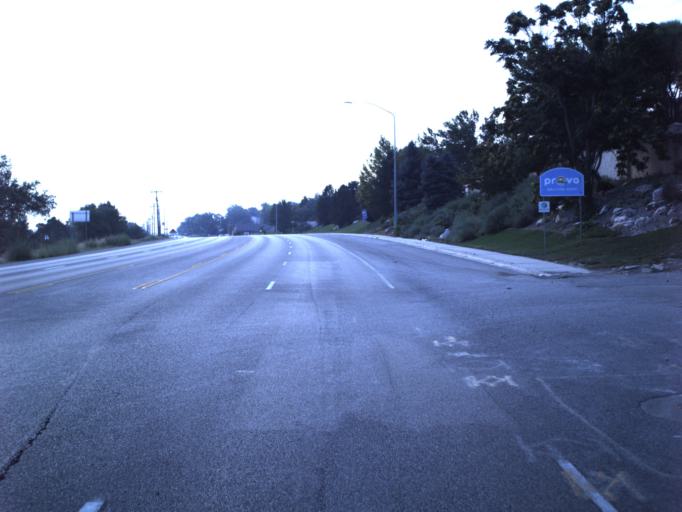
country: US
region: Utah
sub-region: Utah County
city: Springville
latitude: 40.2004
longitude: -111.6200
